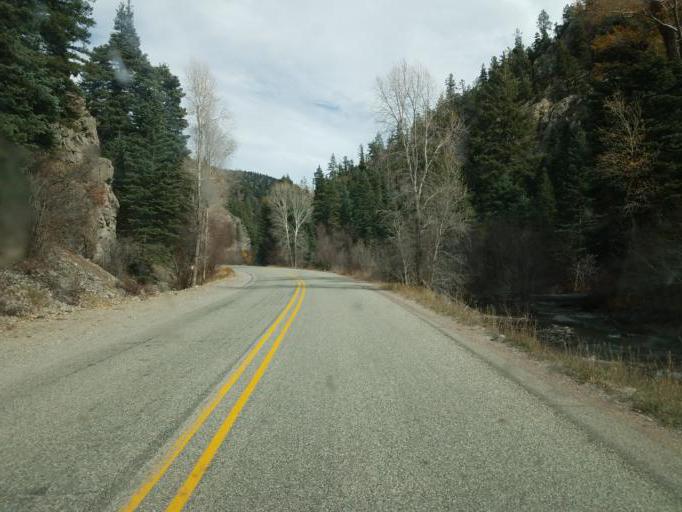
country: US
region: New Mexico
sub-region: Taos County
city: Arroyo Seco
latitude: 36.5634
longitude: -105.5264
